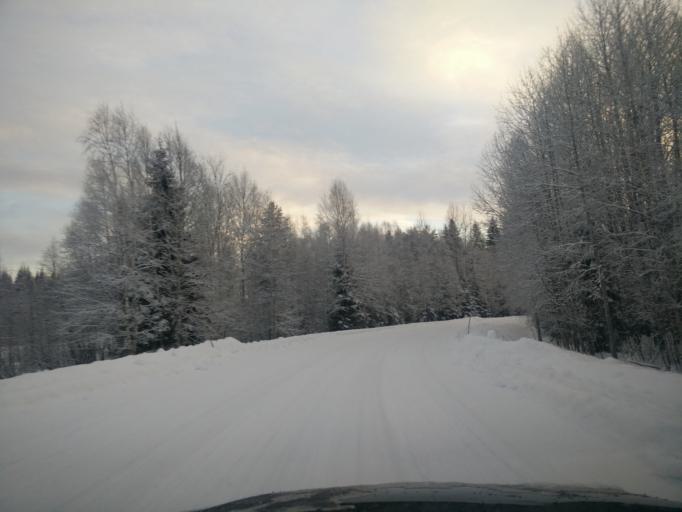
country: SE
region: Vaesternorrland
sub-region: Sundsvalls Kommun
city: Njurundabommen
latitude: 62.2127
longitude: 17.3760
